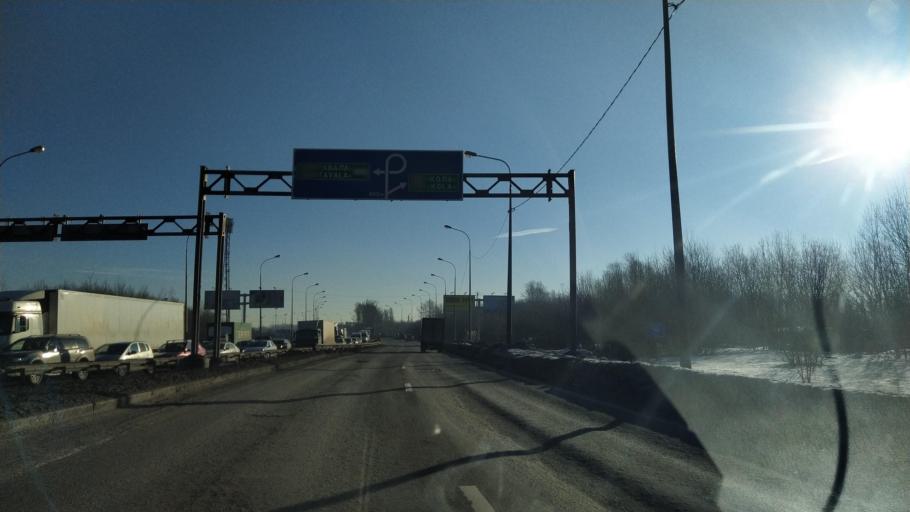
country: RU
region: St.-Petersburg
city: Krasnogvargeisky
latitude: 59.9875
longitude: 30.4713
